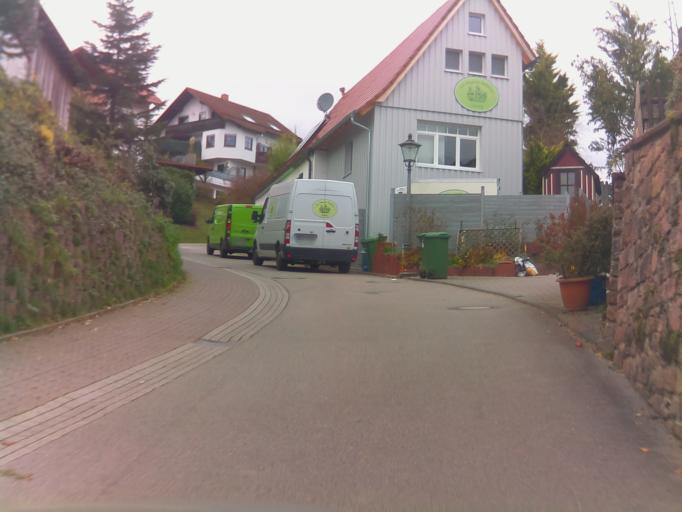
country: DE
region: Baden-Wuerttemberg
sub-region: Karlsruhe Region
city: Heiligkreuzsteinach
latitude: 49.4836
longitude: 8.7939
